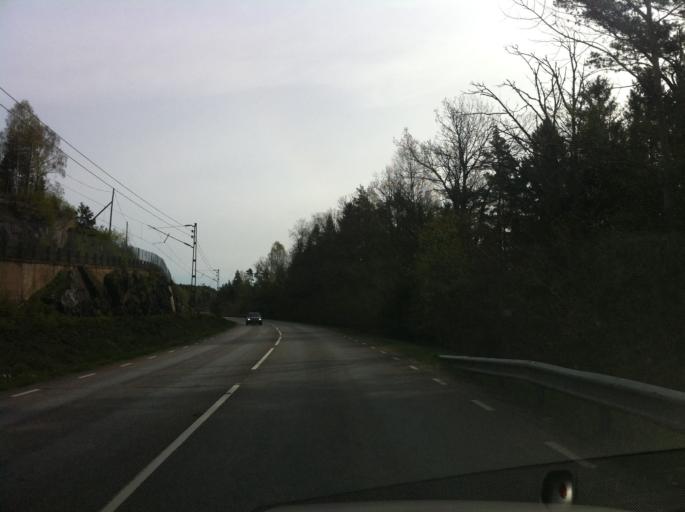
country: SE
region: Vaestra Goetaland
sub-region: Bollebygds Kommun
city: Bollebygd
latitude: 57.6689
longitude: 12.5848
